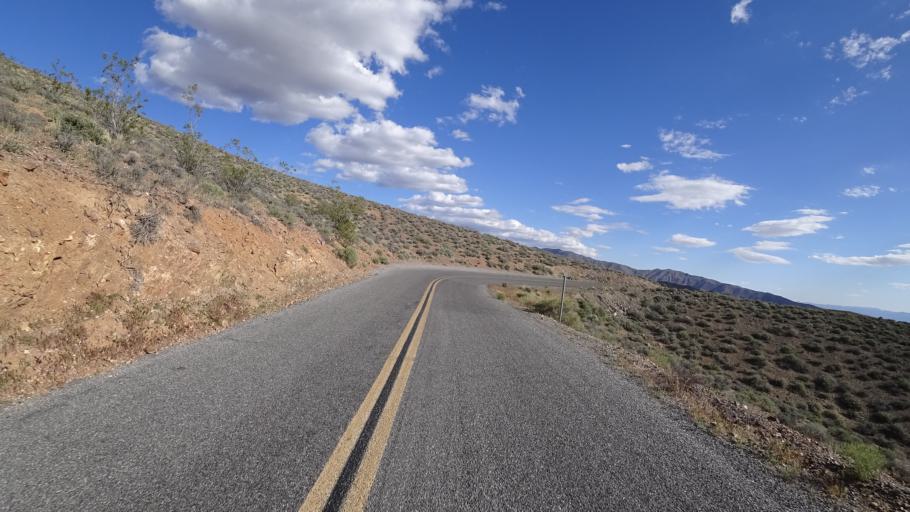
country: US
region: California
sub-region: San Bernardino County
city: Searles Valley
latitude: 36.3185
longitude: -117.1539
